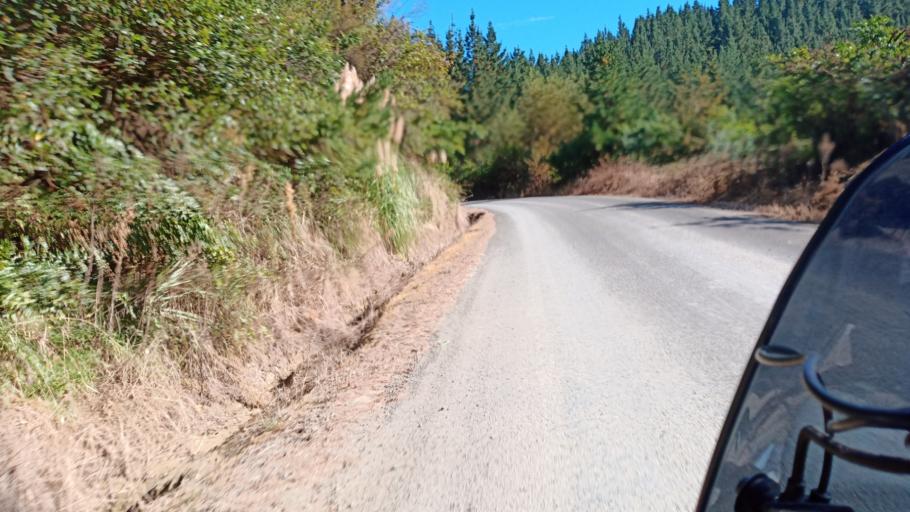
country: NZ
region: Hawke's Bay
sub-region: Wairoa District
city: Wairoa
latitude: -38.9221
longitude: 177.2019
